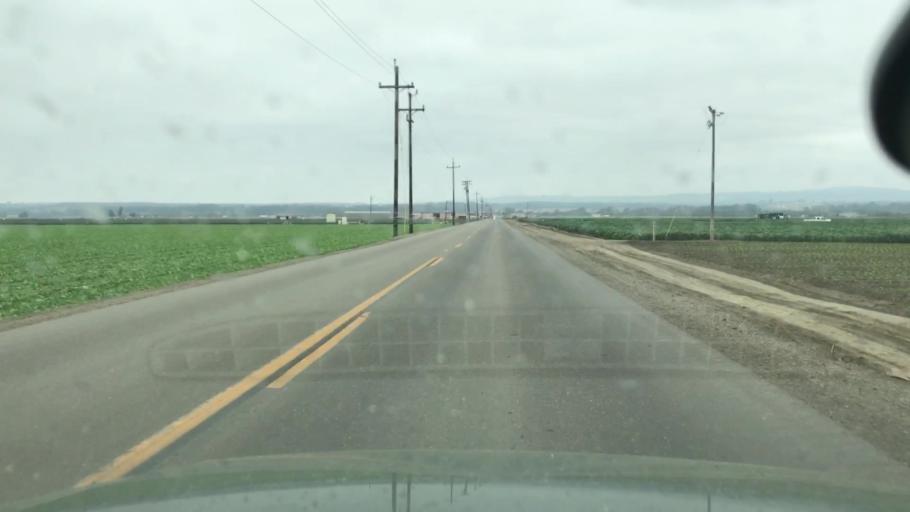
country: US
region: California
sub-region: Santa Barbara County
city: Lompoc
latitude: 34.6428
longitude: -120.4927
